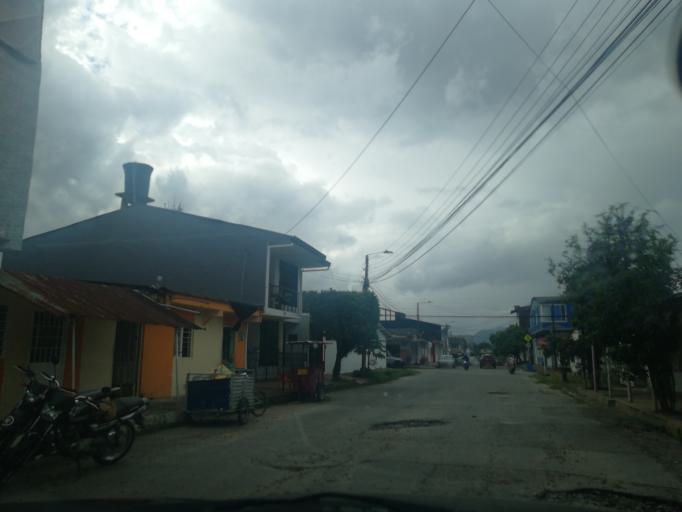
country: CO
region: Meta
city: Acacias
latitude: 3.9861
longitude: -73.7689
